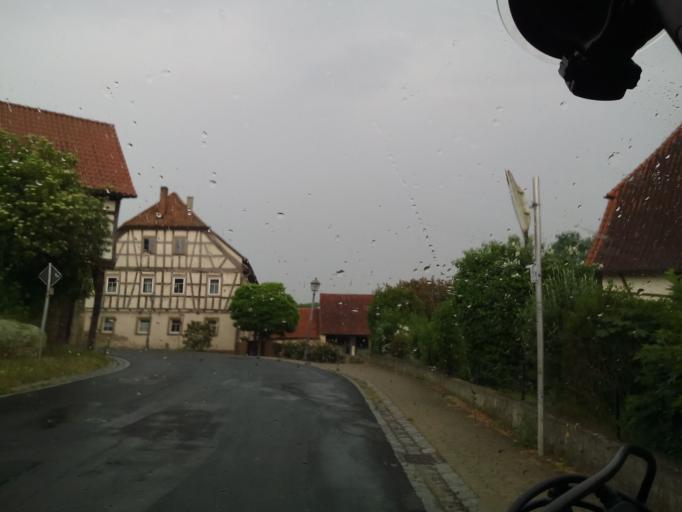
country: DE
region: Bavaria
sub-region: Regierungsbezirk Unterfranken
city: Hochheim
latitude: 50.3638
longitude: 10.4688
